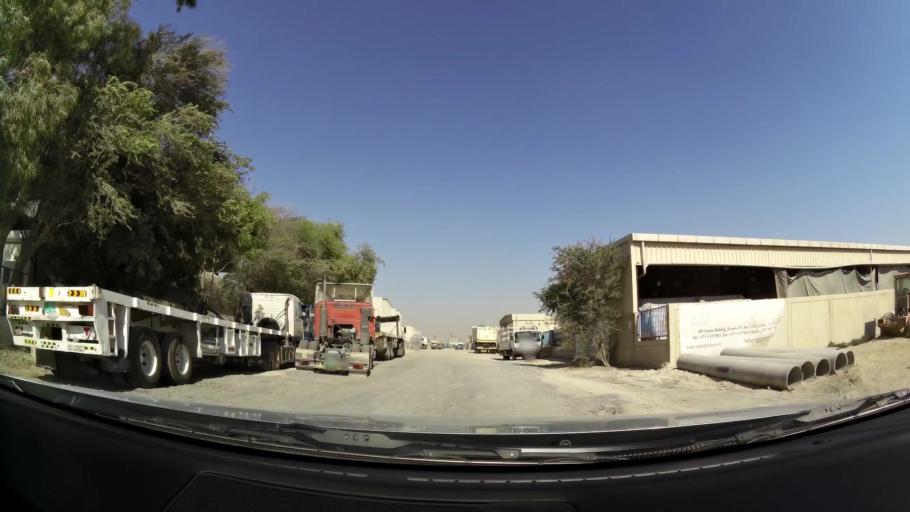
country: AE
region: Dubai
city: Dubai
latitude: 25.0053
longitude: 55.1148
